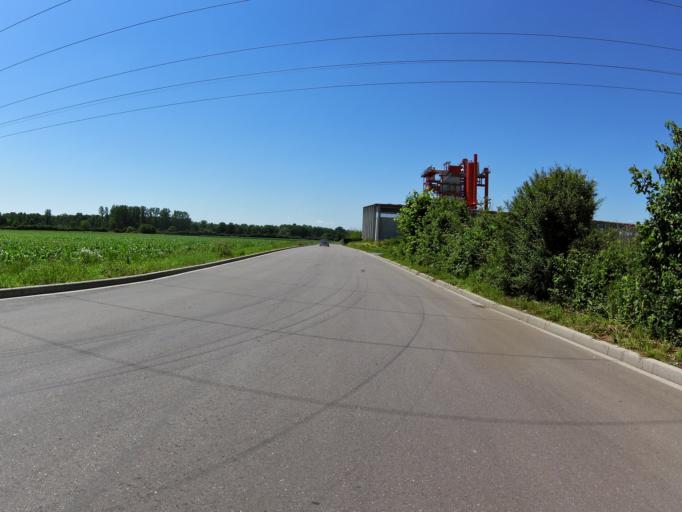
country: DE
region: Baden-Wuerttemberg
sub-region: Freiburg Region
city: Kippenheim
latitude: 48.3426
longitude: 7.8210
